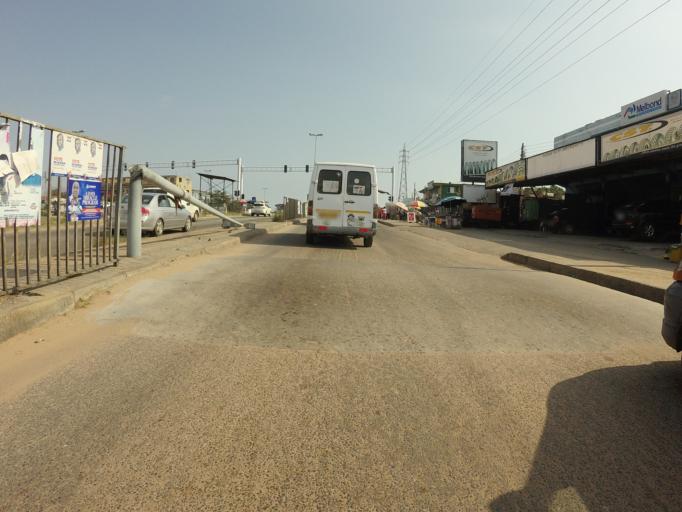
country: GH
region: Greater Accra
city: Gbawe
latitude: 5.5995
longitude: -0.2913
